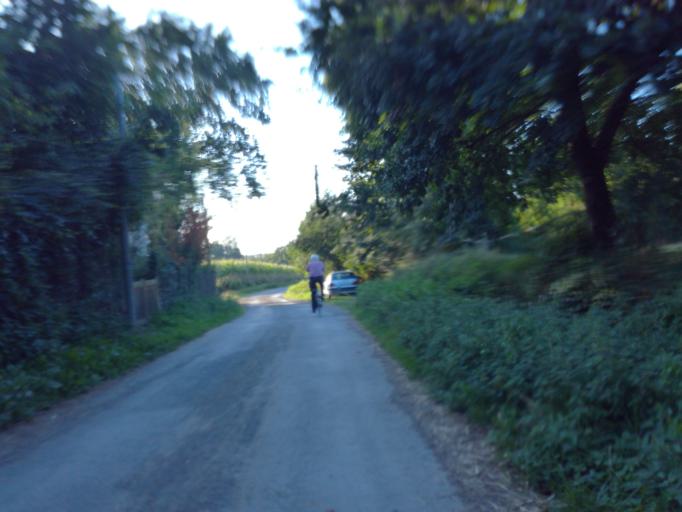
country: FR
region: Brittany
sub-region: Departement d'Ille-et-Vilaine
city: Betton
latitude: 48.1674
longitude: -1.6347
